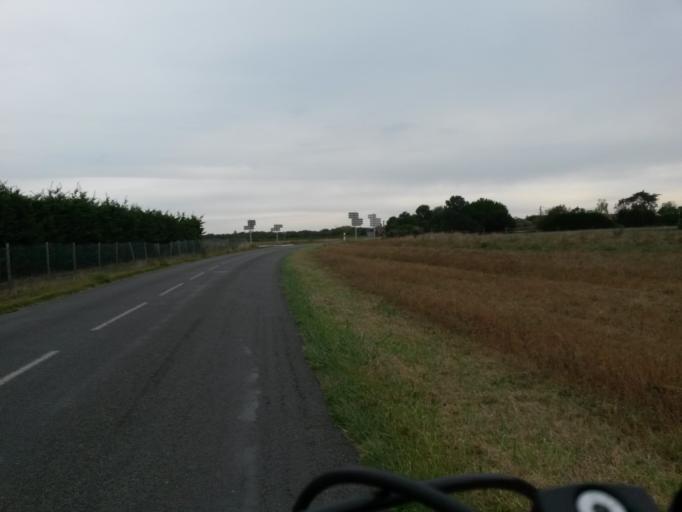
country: FR
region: Poitou-Charentes
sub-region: Departement de la Charente-Maritime
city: Dolus-d'Oleron
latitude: 45.9401
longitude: -1.3404
